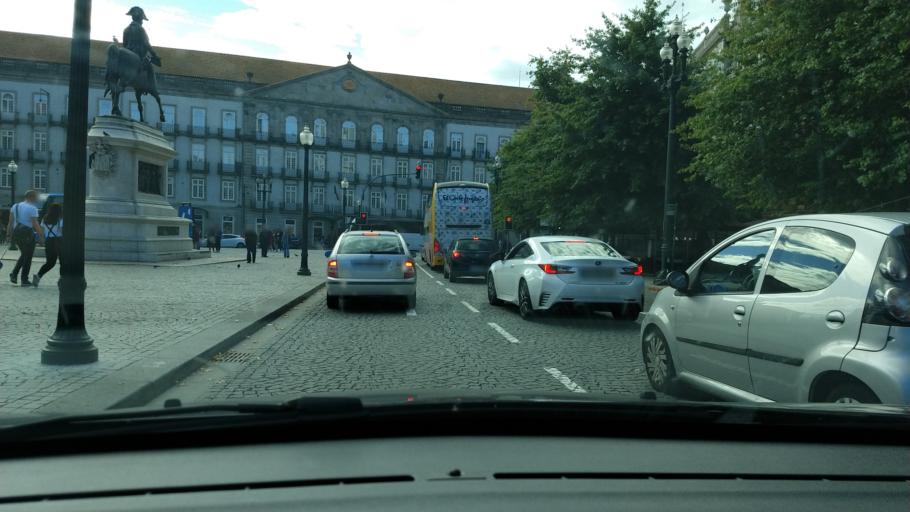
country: PT
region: Porto
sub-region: Porto
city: Porto
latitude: 41.1468
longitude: -8.6114
